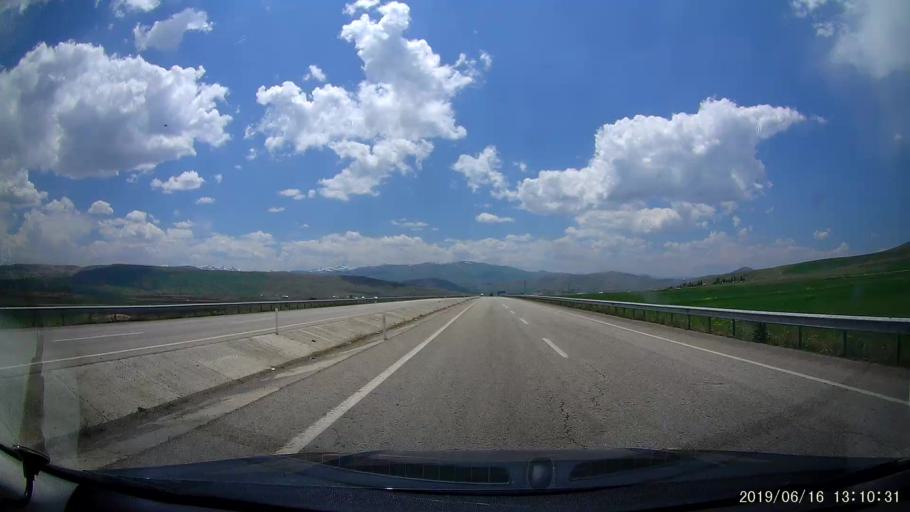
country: TR
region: Agri
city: Diyadin
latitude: 39.5945
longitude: 43.6308
